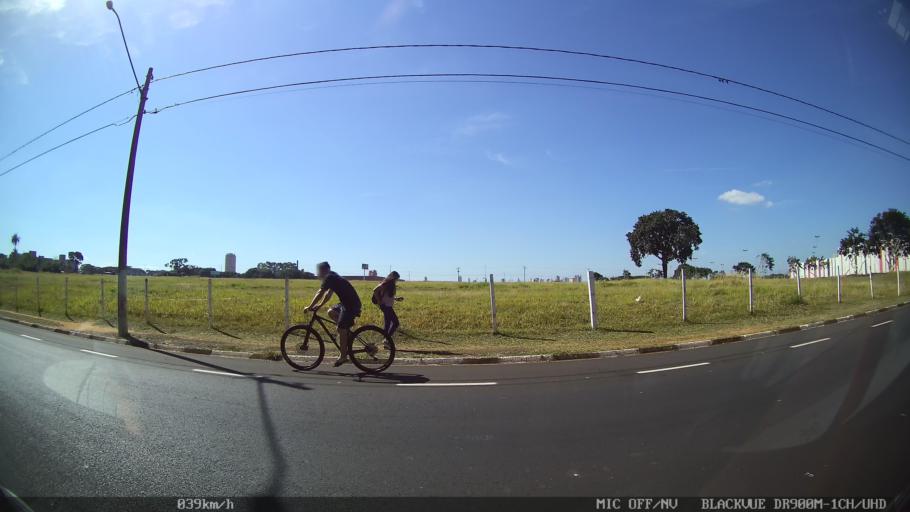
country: BR
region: Sao Paulo
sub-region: Franca
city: Franca
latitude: -20.5466
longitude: -47.4189
